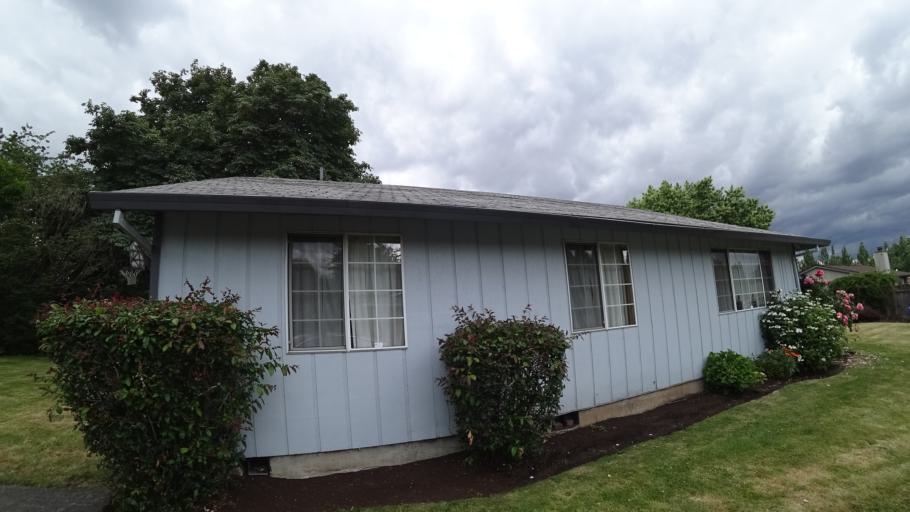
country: US
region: Oregon
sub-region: Multnomah County
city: Portland
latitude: 45.5605
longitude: -122.6108
